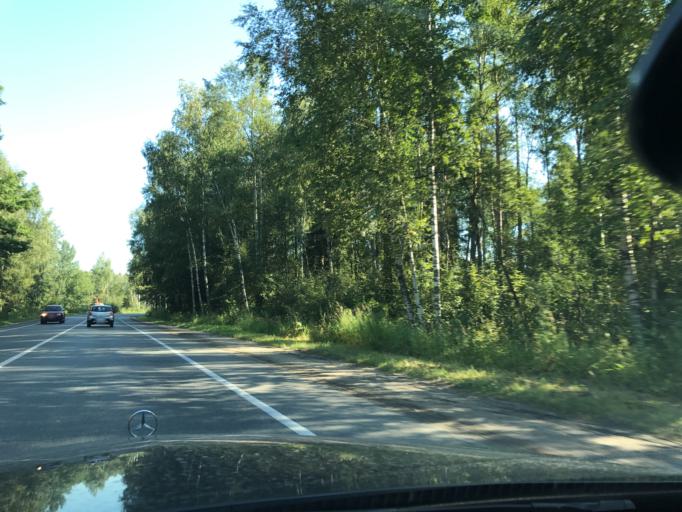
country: RU
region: Moskovskaya
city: Chernogolovka
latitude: 55.9929
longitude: 38.3530
